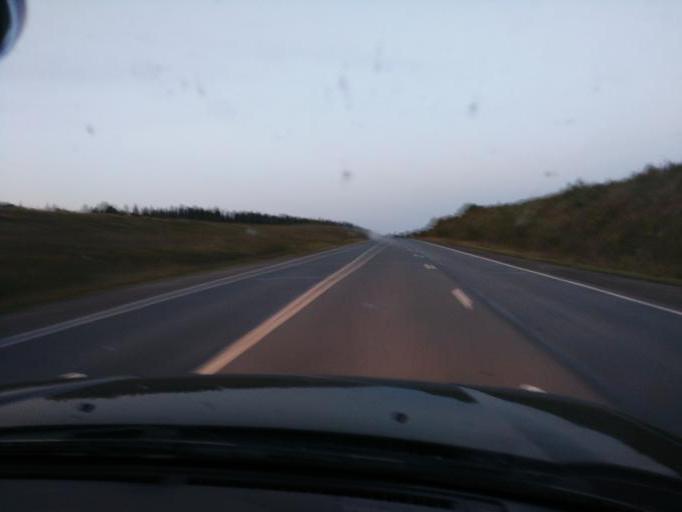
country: RU
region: Perm
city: Verkhnechusovskiye Gorodki
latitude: 58.2248
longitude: 57.1915
